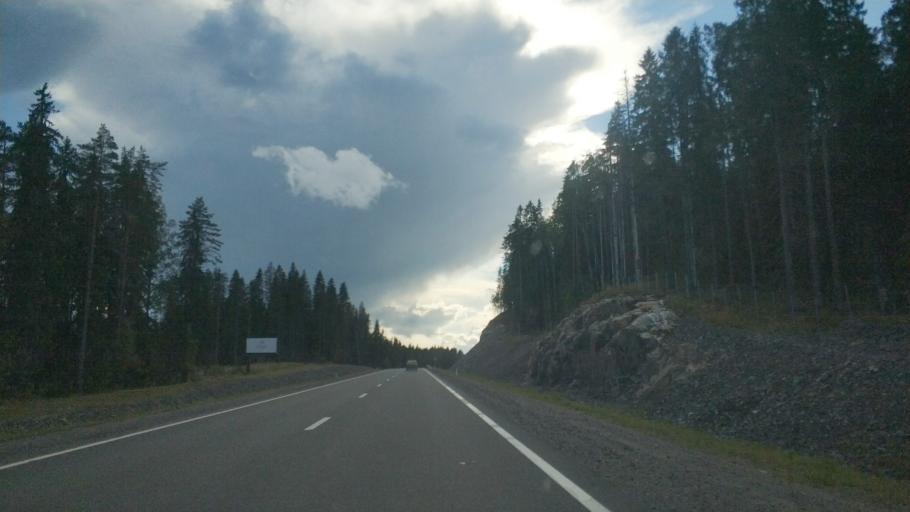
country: RU
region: Republic of Karelia
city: Lakhdenpokh'ya
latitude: 61.5094
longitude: 30.0632
